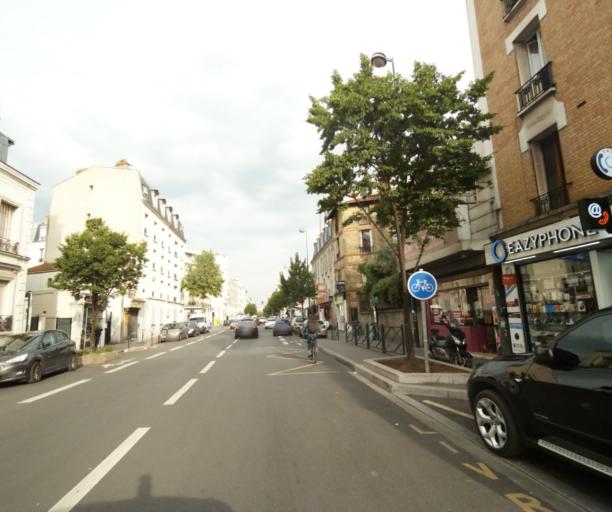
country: FR
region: Ile-de-France
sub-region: Paris
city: Saint-Ouen
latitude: 48.8961
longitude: 2.3364
